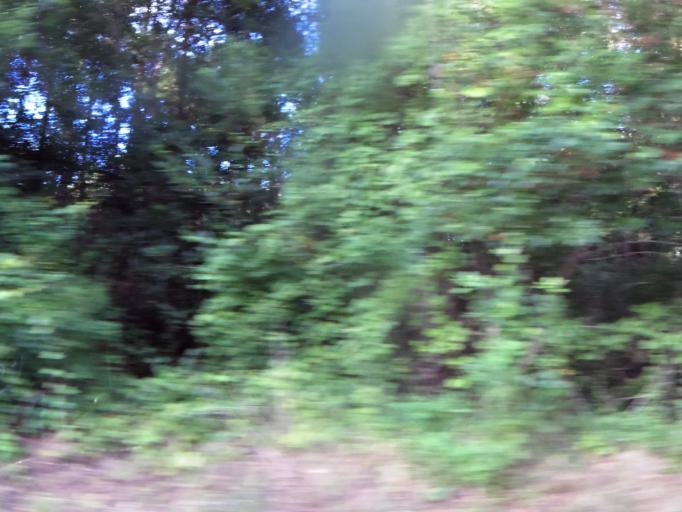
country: US
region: Florida
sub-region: Duval County
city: Jacksonville
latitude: 30.4443
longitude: -81.6819
